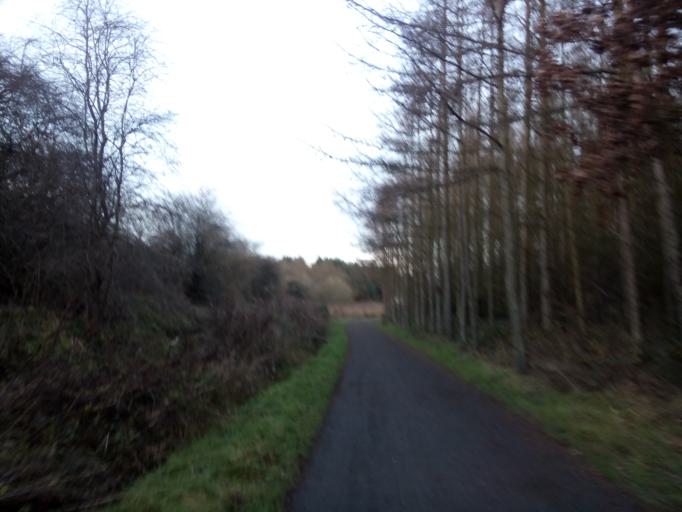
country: GB
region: England
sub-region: County Durham
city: Durham
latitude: 54.7726
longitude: -1.6063
